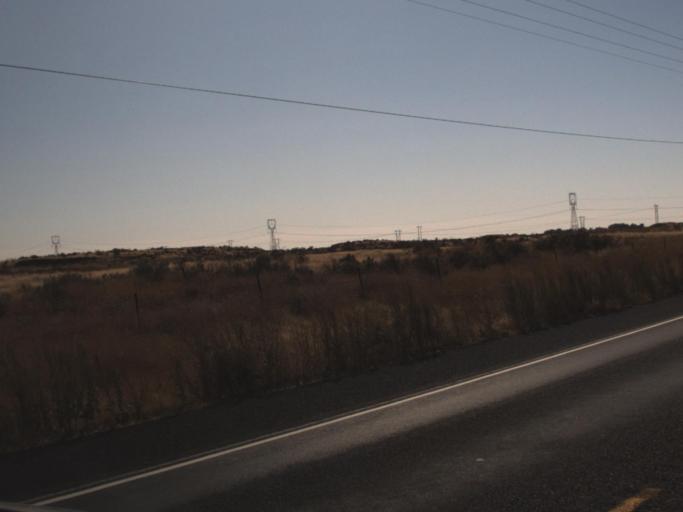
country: US
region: Washington
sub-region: Franklin County
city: Connell
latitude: 46.6497
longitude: -119.0064
